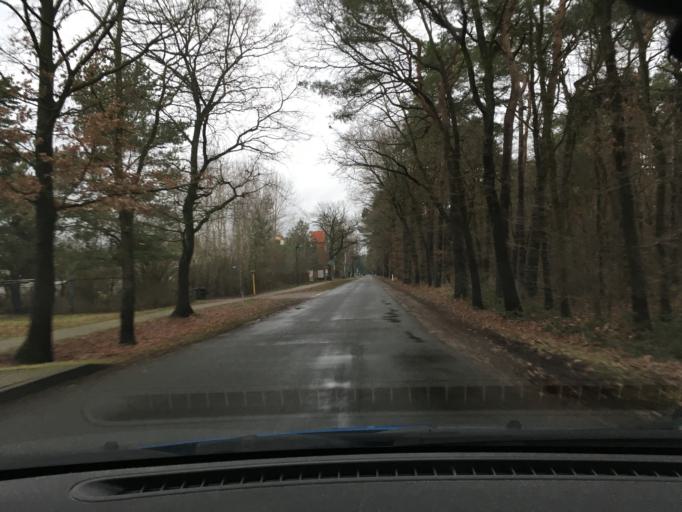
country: DE
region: Mecklenburg-Vorpommern
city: Nostorf
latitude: 53.4323
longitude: 10.6931
